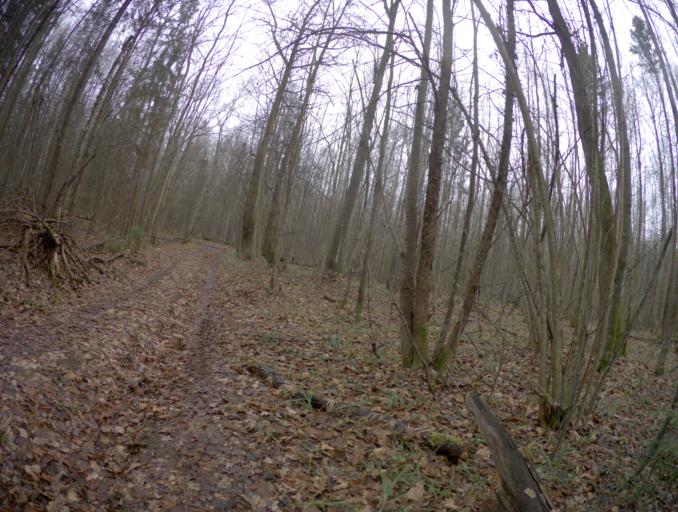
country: RU
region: Vladimir
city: Golovino
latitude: 56.0144
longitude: 40.5349
